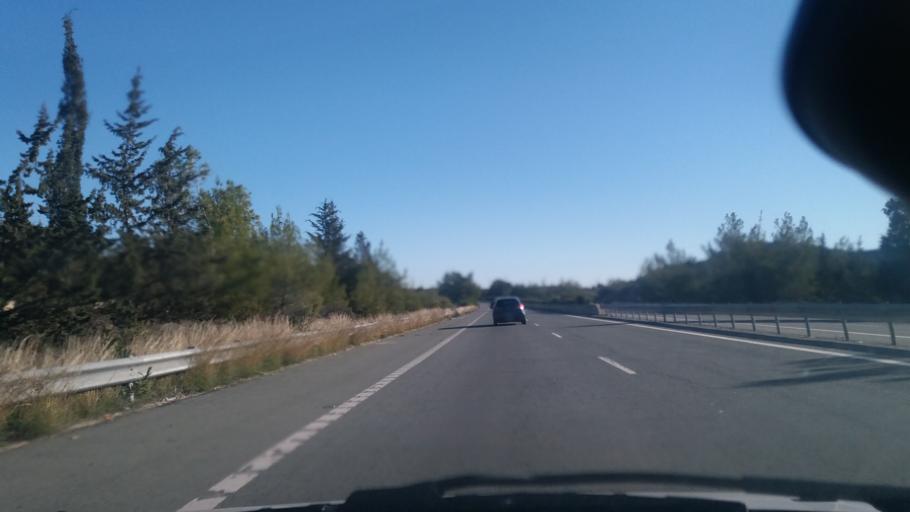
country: CY
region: Larnaka
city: Tersefanou
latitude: 34.8596
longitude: 33.4670
